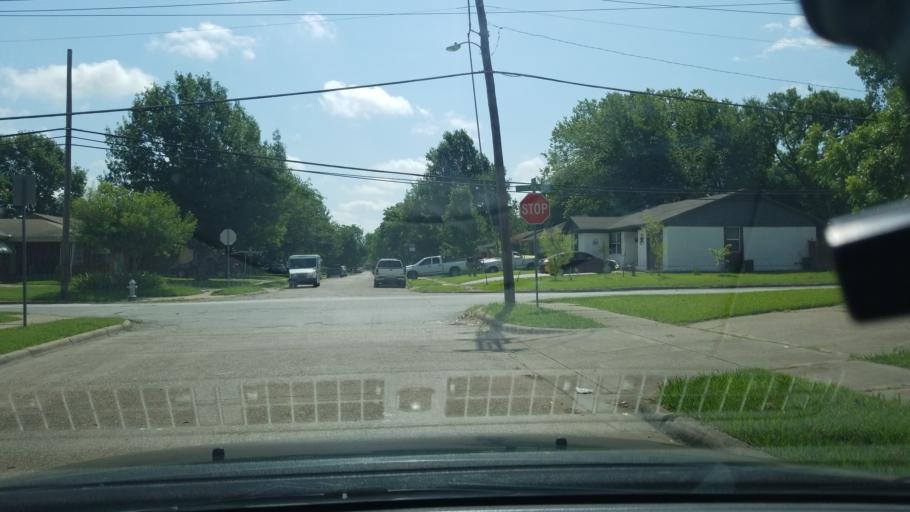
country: US
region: Texas
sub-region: Dallas County
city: Mesquite
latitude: 32.8147
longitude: -96.6537
